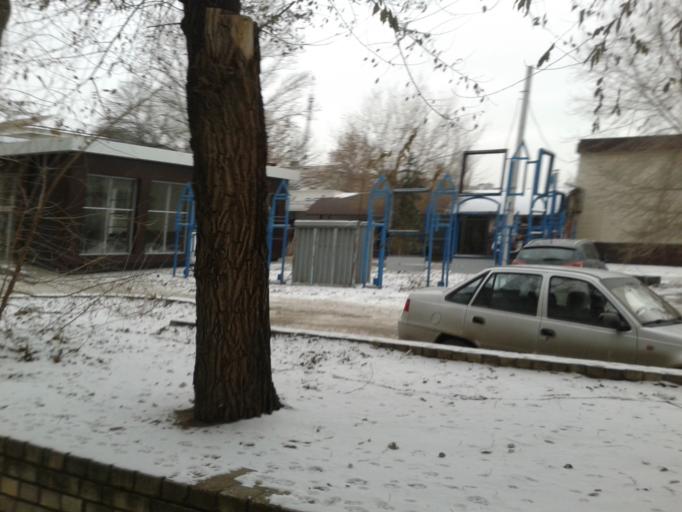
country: RU
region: Volgograd
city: Volgograd
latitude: 48.7079
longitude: 44.5087
